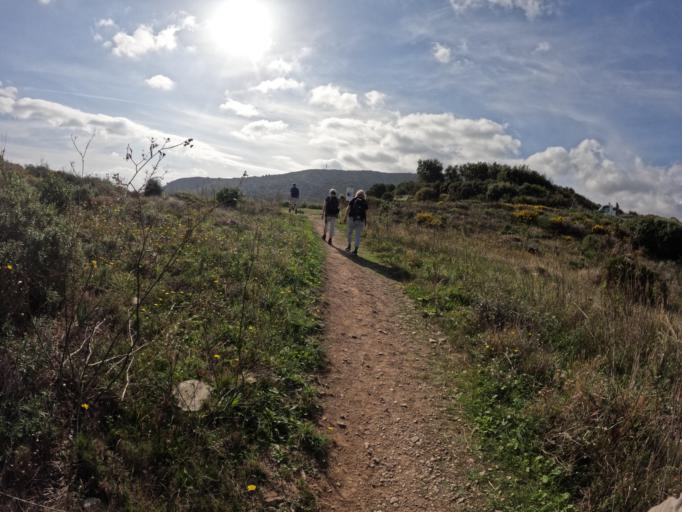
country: FR
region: Languedoc-Roussillon
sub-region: Departement des Pyrenees-Orientales
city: Banyuls de la Marenda
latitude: 42.4755
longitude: 3.1523
